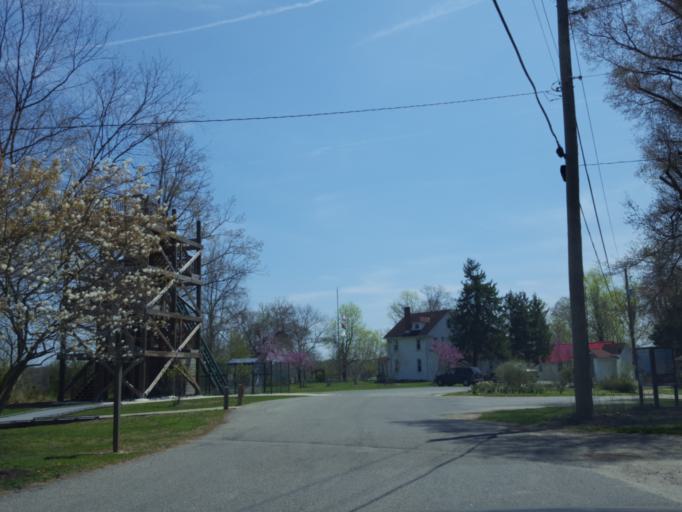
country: US
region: Maryland
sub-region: Prince George's County
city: Croom
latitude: 38.7736
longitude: -76.7112
